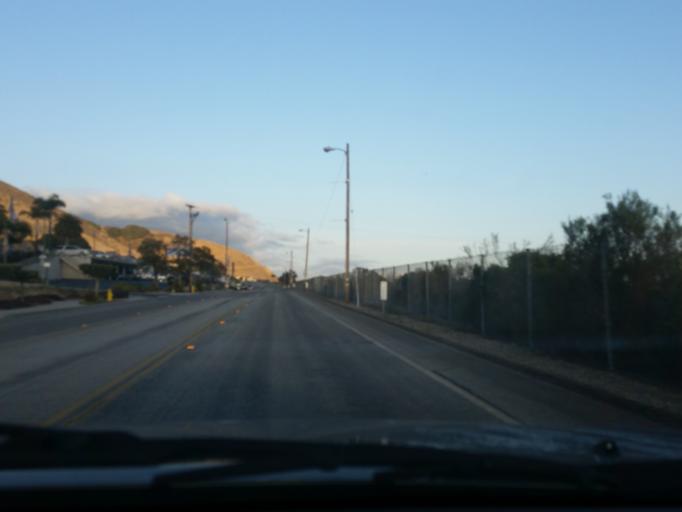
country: US
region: California
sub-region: San Luis Obispo County
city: Pismo Beach
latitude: 35.1576
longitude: -120.6703
